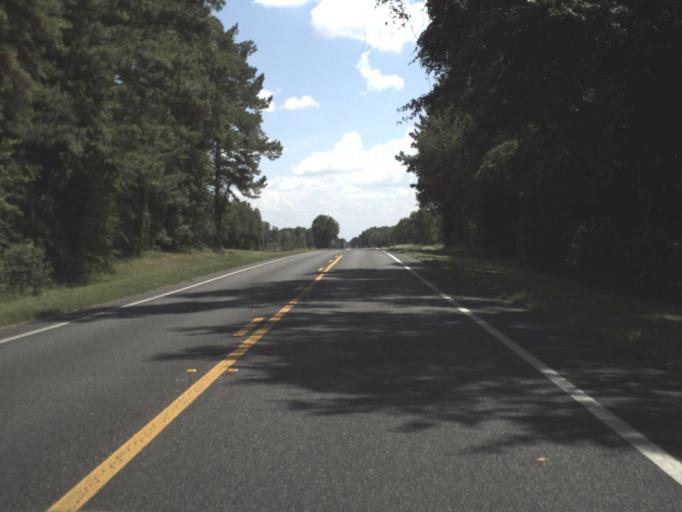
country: US
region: Florida
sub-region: Alachua County
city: High Springs
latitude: 29.9187
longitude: -82.6094
